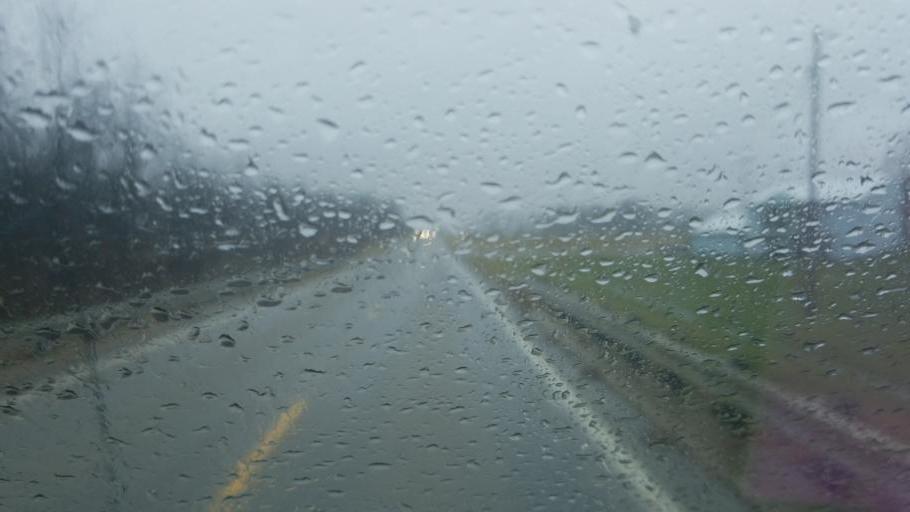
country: US
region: Ohio
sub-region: Morrow County
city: Mount Gilead
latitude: 40.5981
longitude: -82.7663
